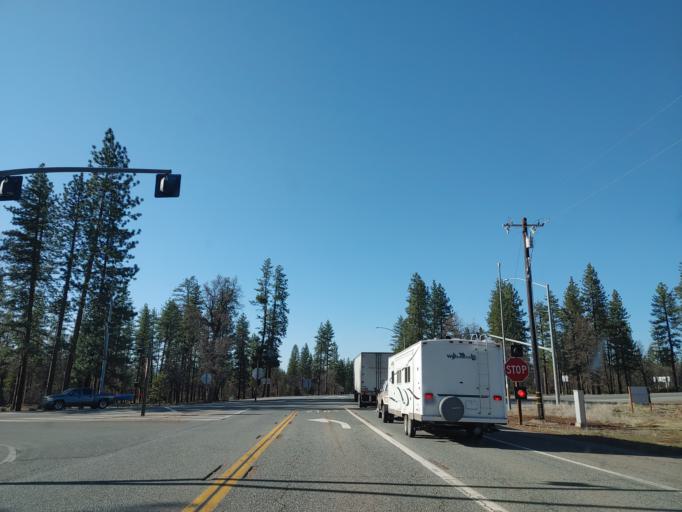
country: US
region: California
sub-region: Shasta County
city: Burney
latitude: 40.9378
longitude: -121.6064
